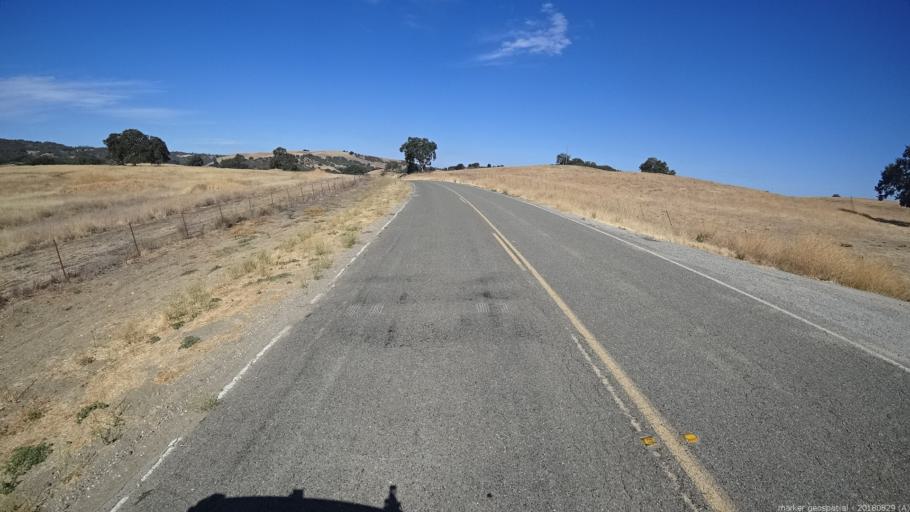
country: US
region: California
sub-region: San Luis Obispo County
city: Lake Nacimiento
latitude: 35.8363
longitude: -121.0304
